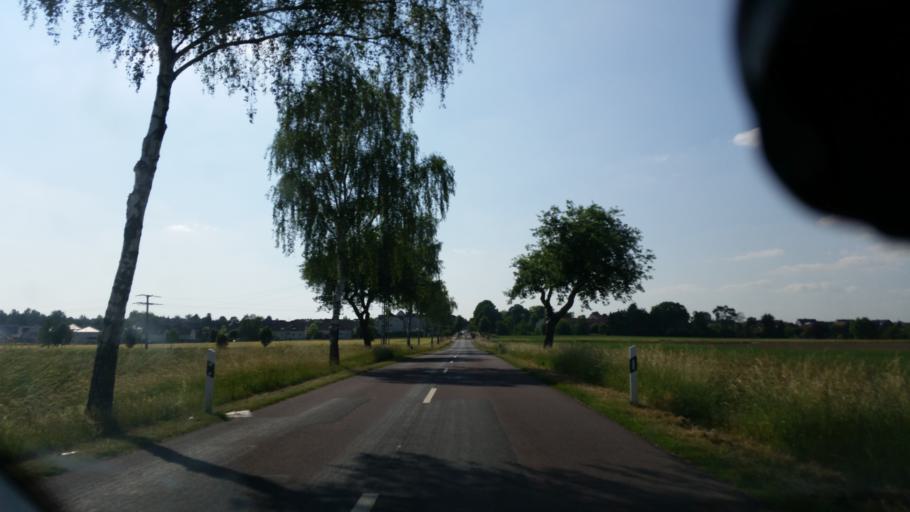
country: DE
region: Lower Saxony
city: Lehre
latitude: 52.3223
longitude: 10.6795
